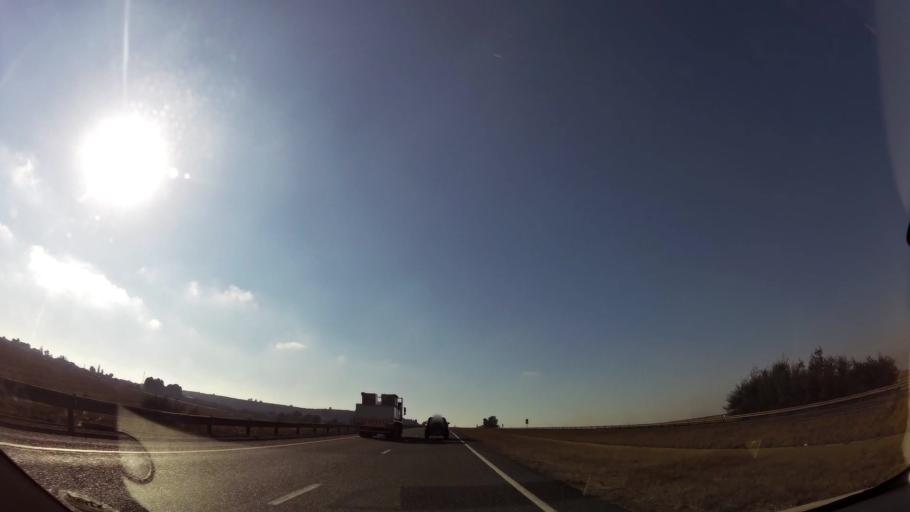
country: ZA
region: Gauteng
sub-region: City of Tshwane Metropolitan Municipality
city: Bronkhorstspruit
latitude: -26.0167
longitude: 28.9570
